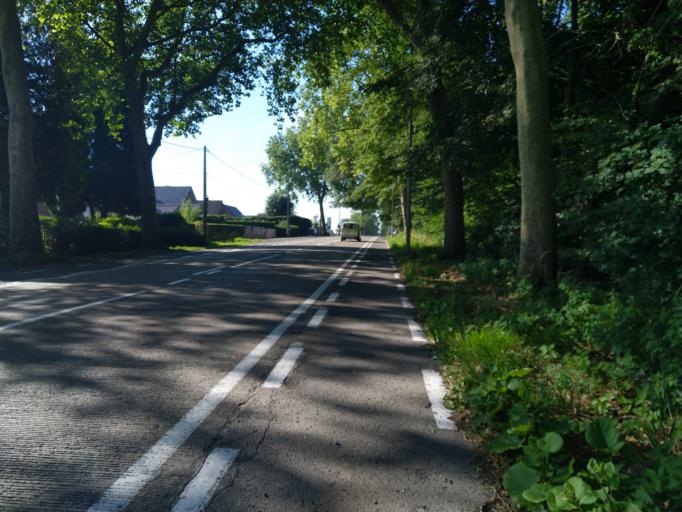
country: BE
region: Wallonia
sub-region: Province du Hainaut
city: Chasse Royale
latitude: 50.4159
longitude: 3.9537
